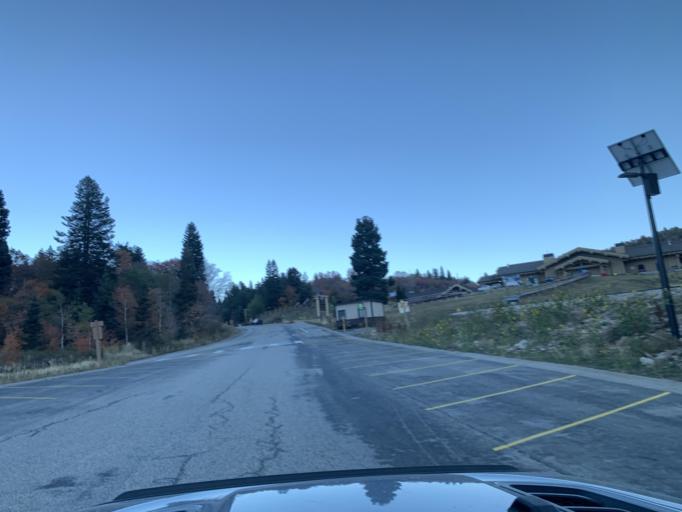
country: US
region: Utah
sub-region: Weber County
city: Uintah
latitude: 41.2172
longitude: -111.8607
